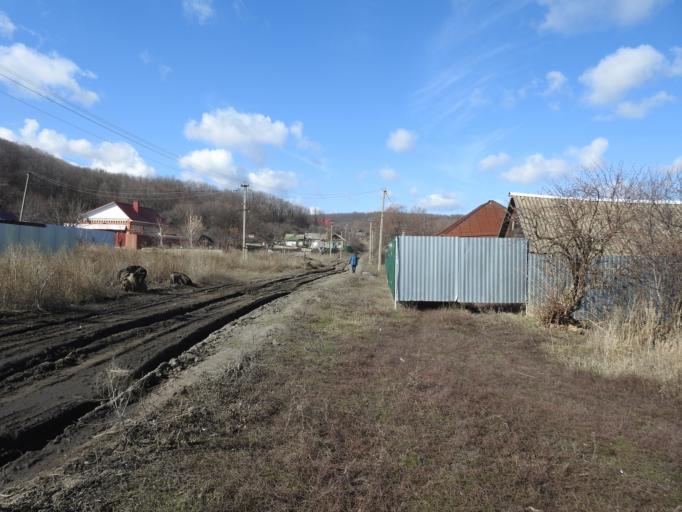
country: RU
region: Saratov
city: Krasnyy Oktyabr'
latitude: 51.3821
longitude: 45.7470
